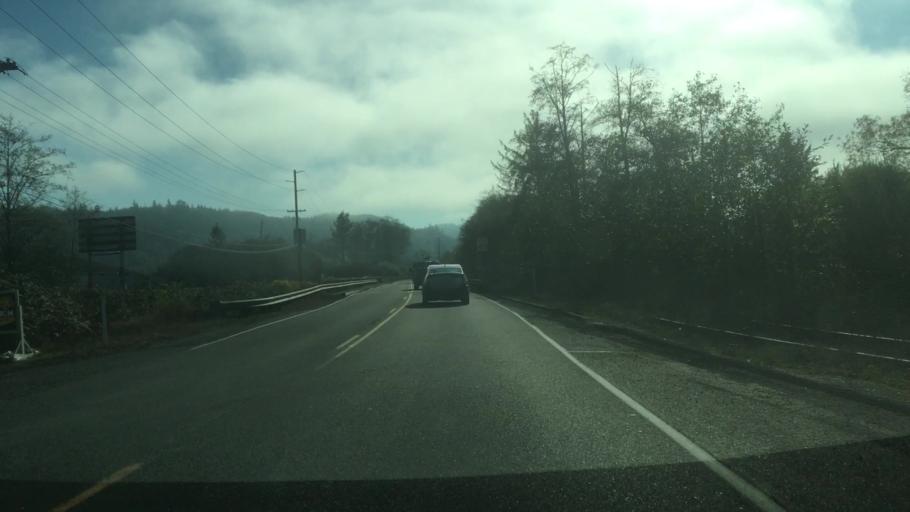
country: US
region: Washington
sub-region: Grays Harbor County
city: Montesano
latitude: 46.9742
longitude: -123.6010
